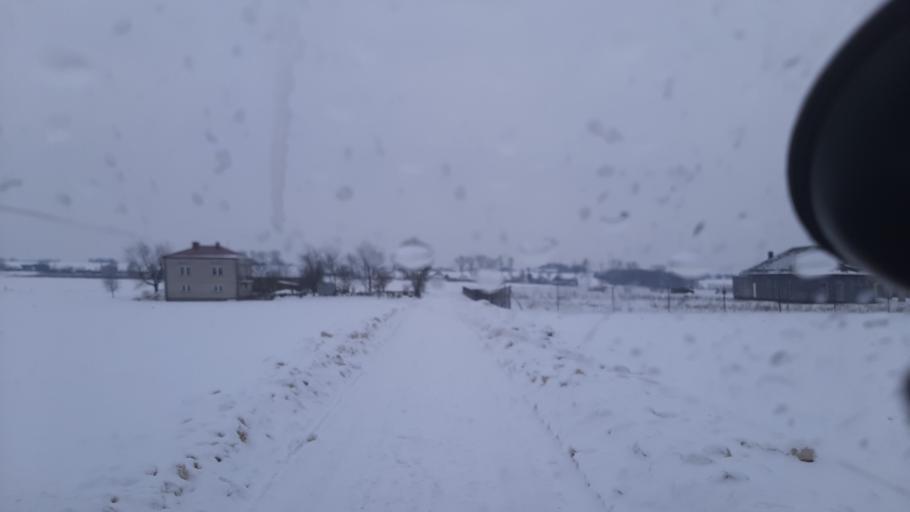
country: PL
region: Lublin Voivodeship
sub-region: Powiat lubelski
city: Jastkow
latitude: 51.3508
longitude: 22.4002
